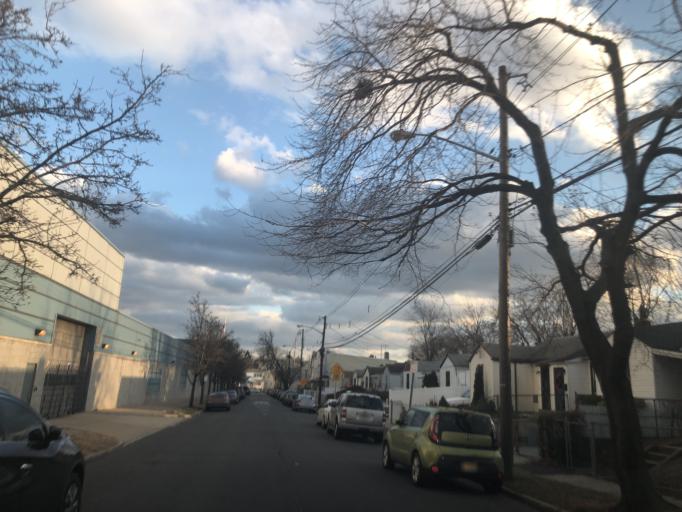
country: US
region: New Jersey
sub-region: Hudson County
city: Bayonne
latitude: 40.6926
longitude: -74.0986
